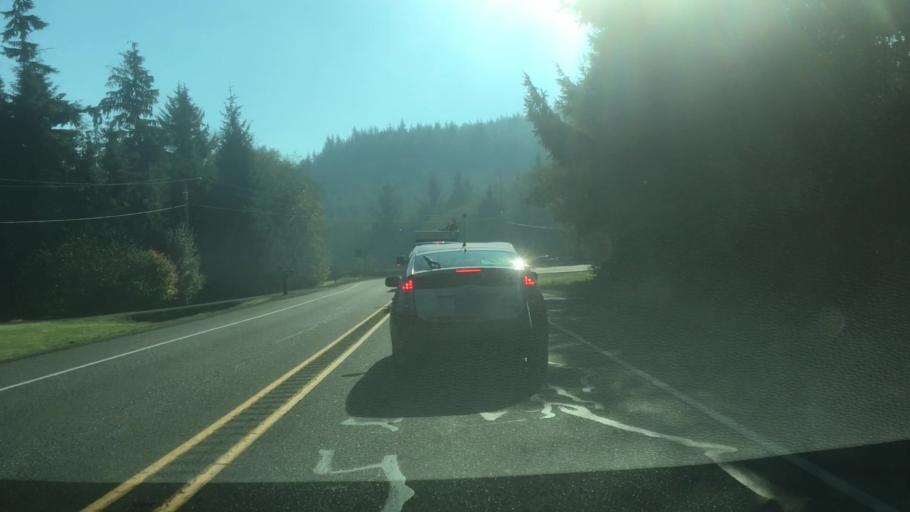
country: US
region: Washington
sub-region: Grays Harbor County
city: Central Park
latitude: 46.9193
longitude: -123.7185
